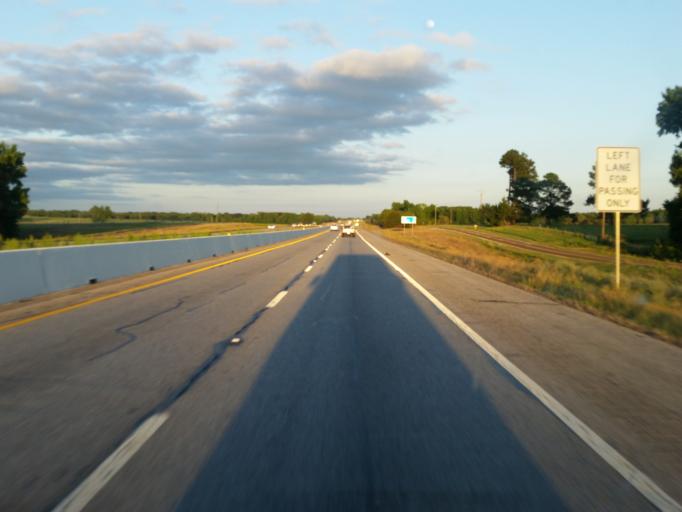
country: US
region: Texas
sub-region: Van Zandt County
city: Van
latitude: 32.5386
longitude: -95.7468
